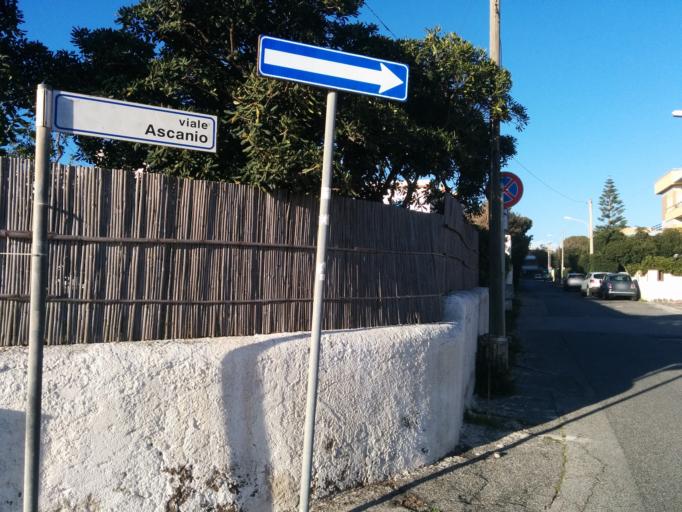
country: IT
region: Latium
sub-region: Citta metropolitana di Roma Capitale
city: Lavinio
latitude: 41.4973
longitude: 12.5854
